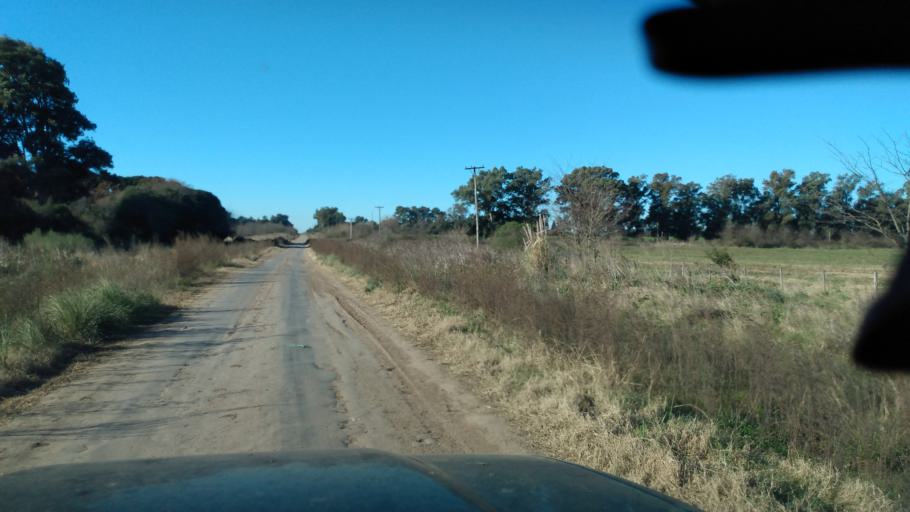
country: AR
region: Buenos Aires
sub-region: Partido de Lujan
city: Lujan
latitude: -34.5640
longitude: -59.1675
